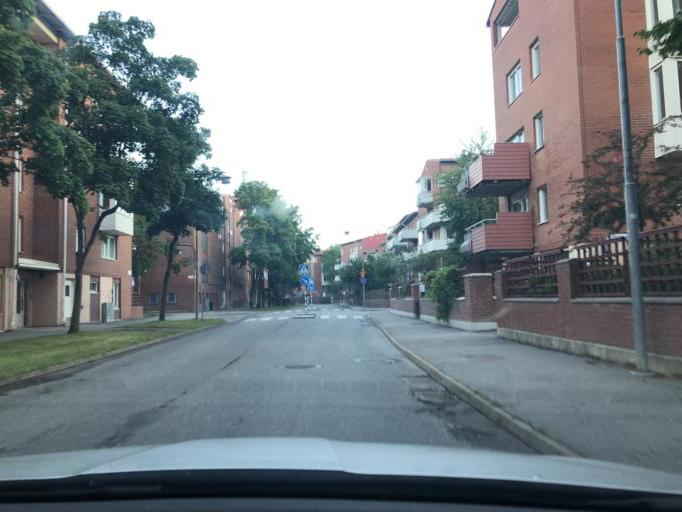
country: SE
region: Stockholm
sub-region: Nacka Kommun
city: Alta
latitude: 59.2675
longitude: 18.1375
